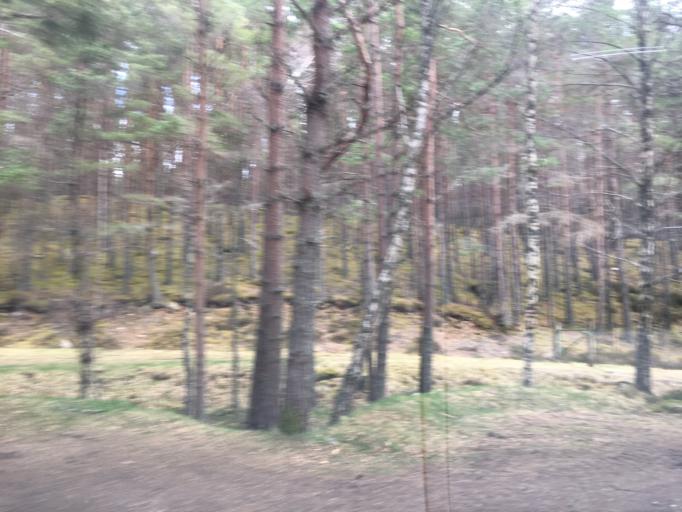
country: GB
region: Scotland
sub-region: Highland
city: Kingussie
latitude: 57.0966
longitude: -3.9244
